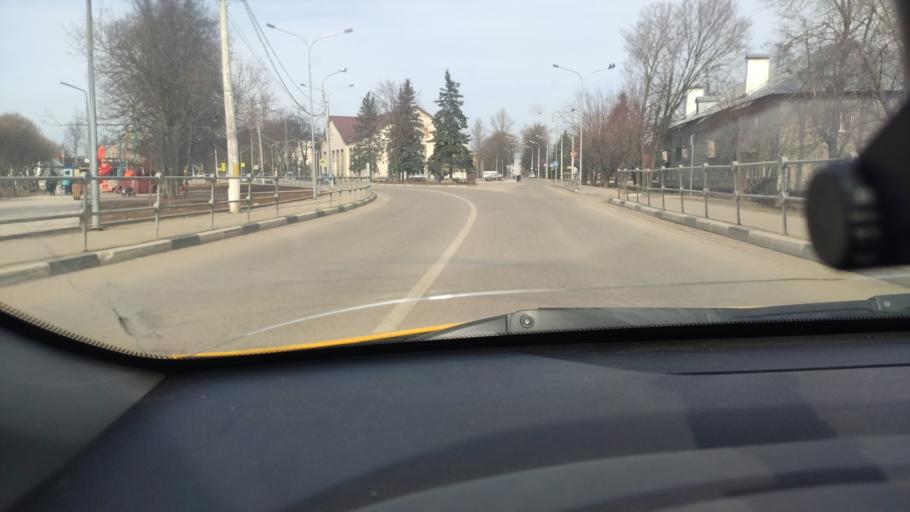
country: RU
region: Moskovskaya
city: Ruza
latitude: 55.7033
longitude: 36.1904
